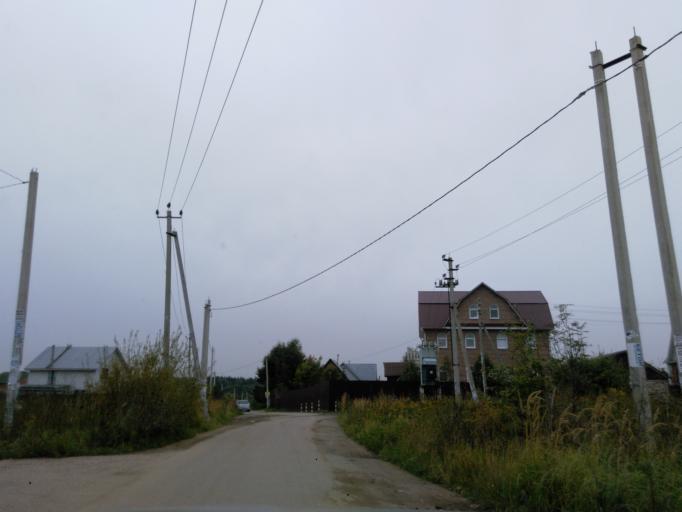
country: RU
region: Moskovskaya
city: Lozhki
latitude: 56.0671
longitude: 37.1161
